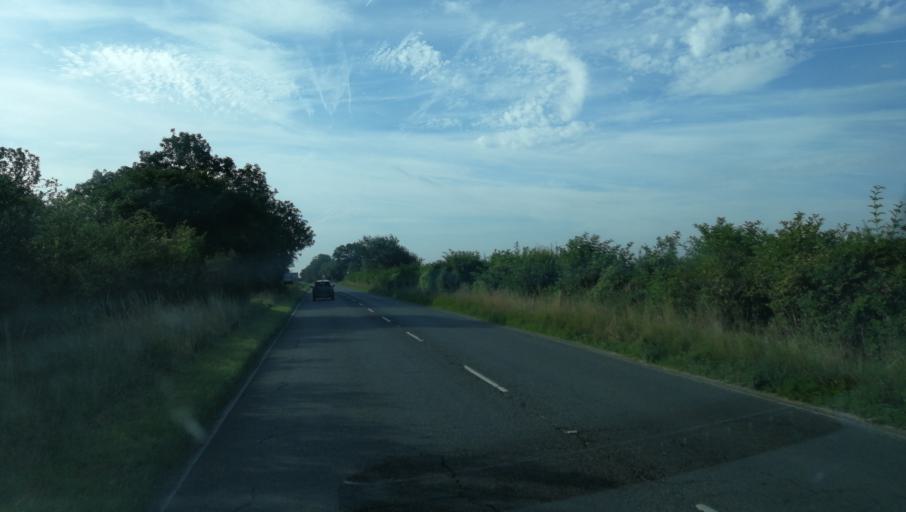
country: GB
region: England
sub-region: Oxfordshire
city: Woodstock
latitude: 51.8655
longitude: -1.3256
